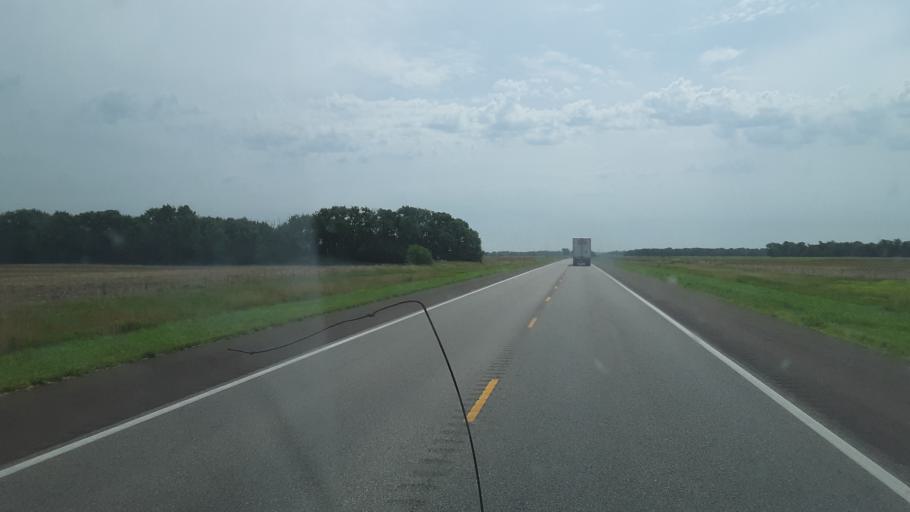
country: US
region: Kansas
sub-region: Reno County
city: Nickerson
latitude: 37.9853
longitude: -98.1703
